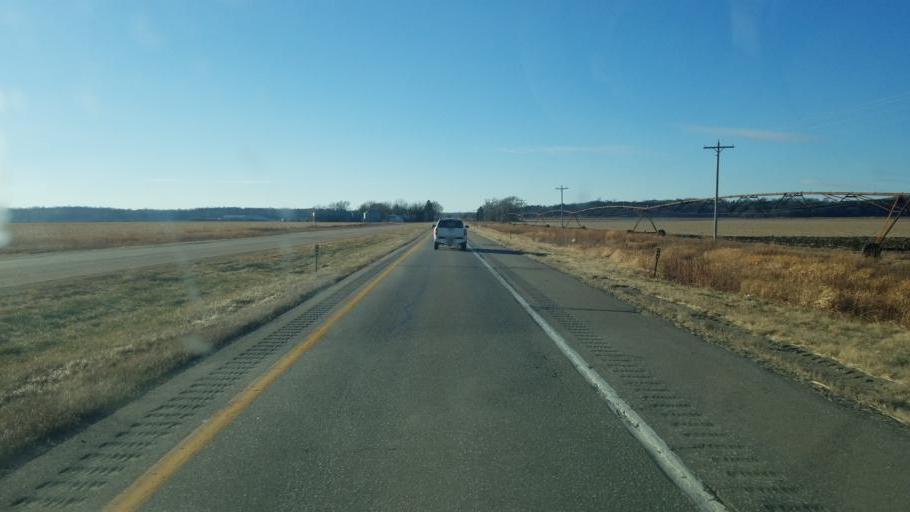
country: US
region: South Dakota
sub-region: Union County
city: Dakota Dunes
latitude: 42.4484
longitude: -96.5428
